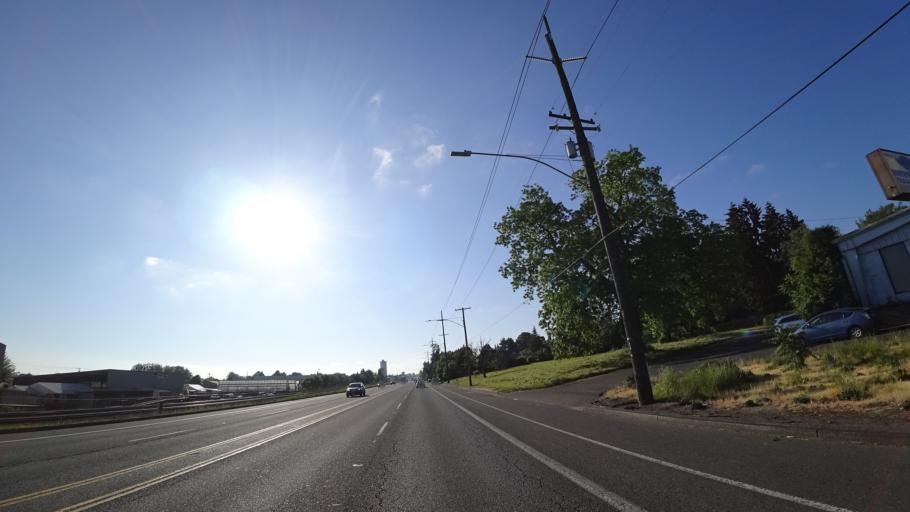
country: US
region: Oregon
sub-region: Multnomah County
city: Portland
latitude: 45.5760
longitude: -122.6486
